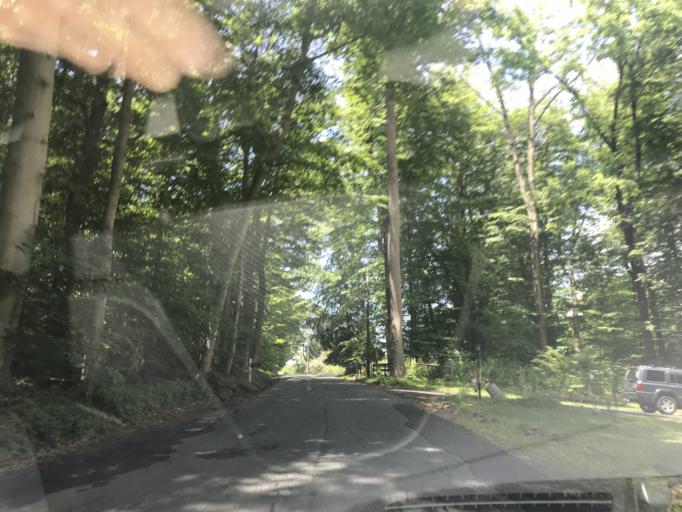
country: US
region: Maryland
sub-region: Baltimore County
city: Kingsville
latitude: 39.4717
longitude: -76.4349
